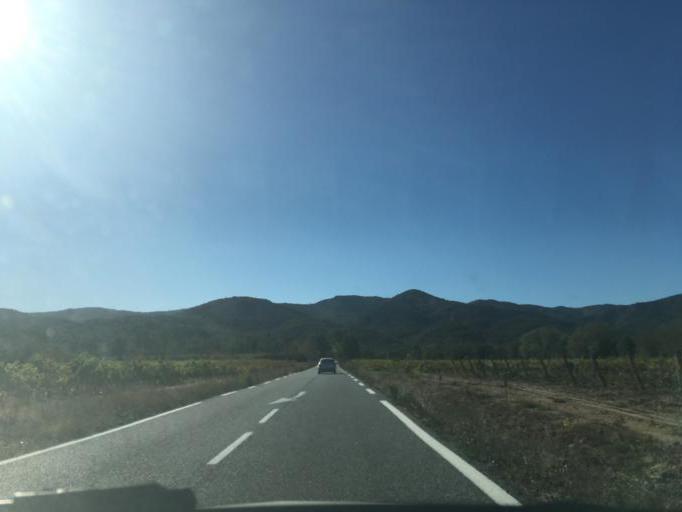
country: FR
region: Provence-Alpes-Cote d'Azur
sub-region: Departement du Var
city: La Garde-Freinet
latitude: 43.3408
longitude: 6.4278
